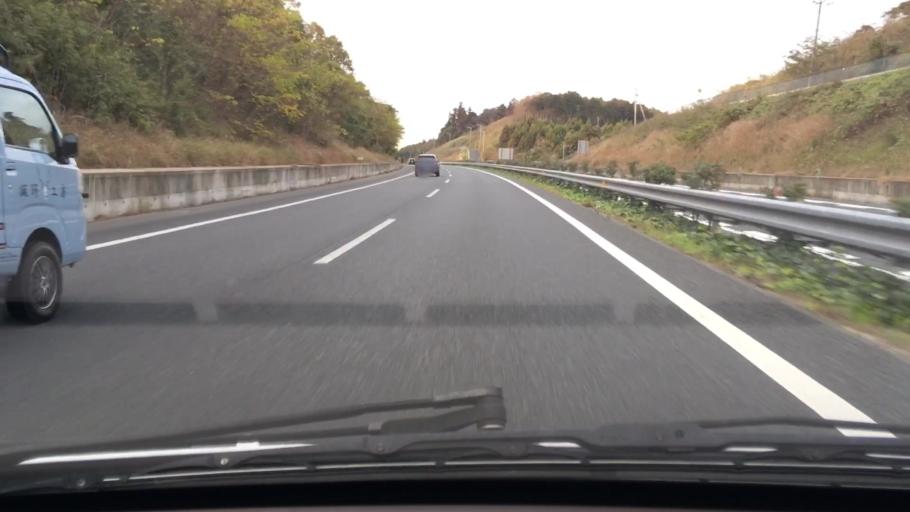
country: JP
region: Chiba
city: Kisarazu
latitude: 35.3279
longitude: 139.9463
